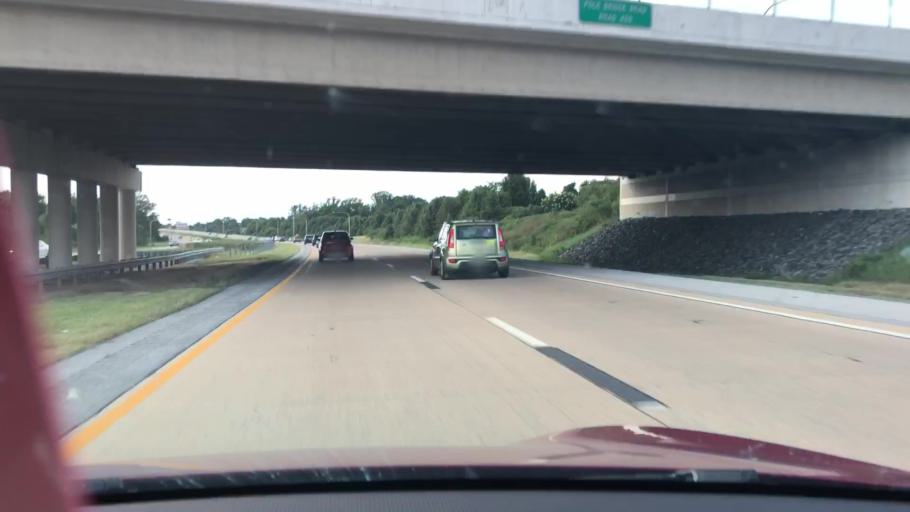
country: US
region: Delaware
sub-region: New Castle County
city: Middletown
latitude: 39.5000
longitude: -75.6461
